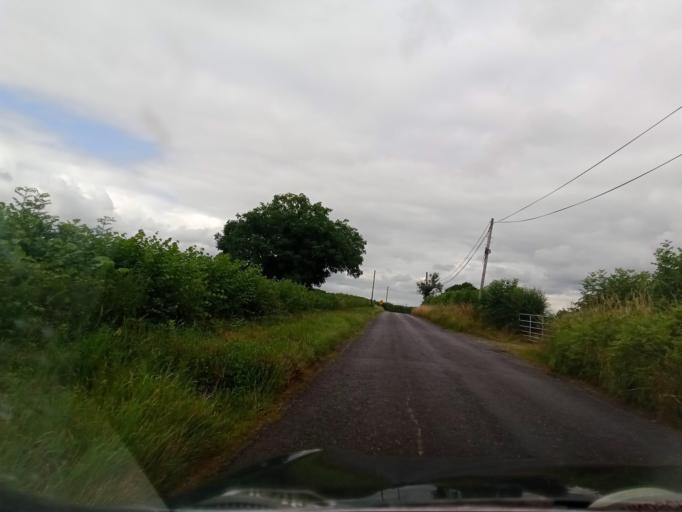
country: IE
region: Leinster
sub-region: Laois
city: Stradbally
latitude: 52.9906
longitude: -7.1798
